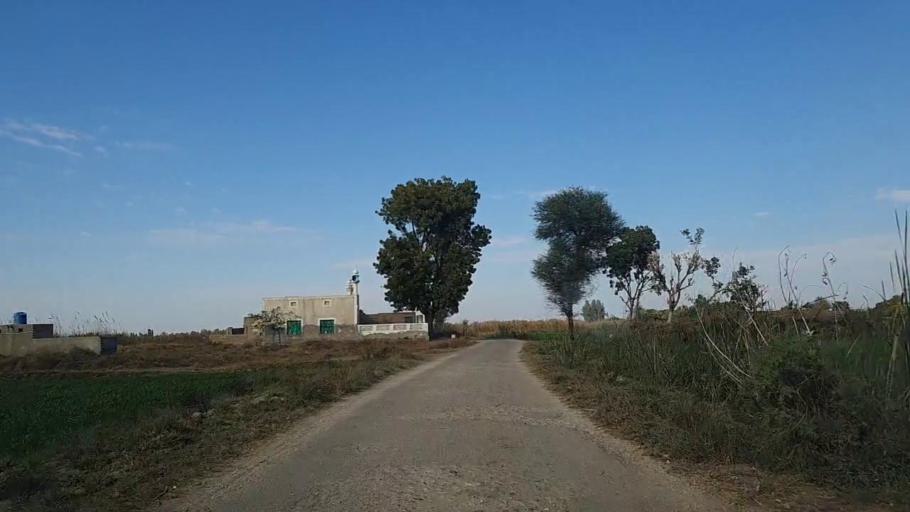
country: PK
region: Sindh
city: Khadro
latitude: 26.2946
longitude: 68.8202
